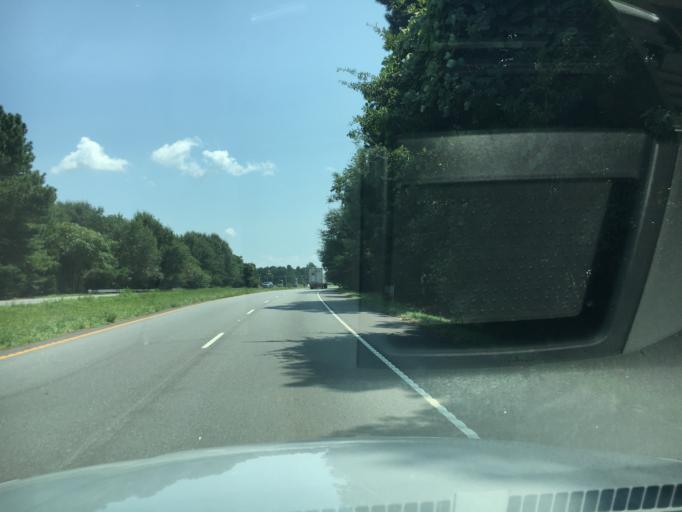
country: US
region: South Carolina
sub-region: Anderson County
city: Pendleton
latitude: 34.6379
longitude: -82.7869
